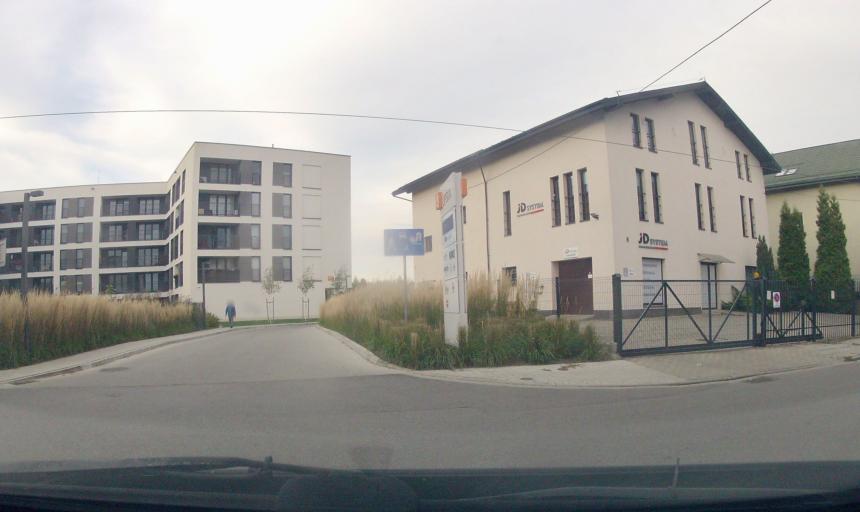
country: PL
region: Lesser Poland Voivodeship
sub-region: Krakow
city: Krakow
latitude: 50.0394
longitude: 19.9858
